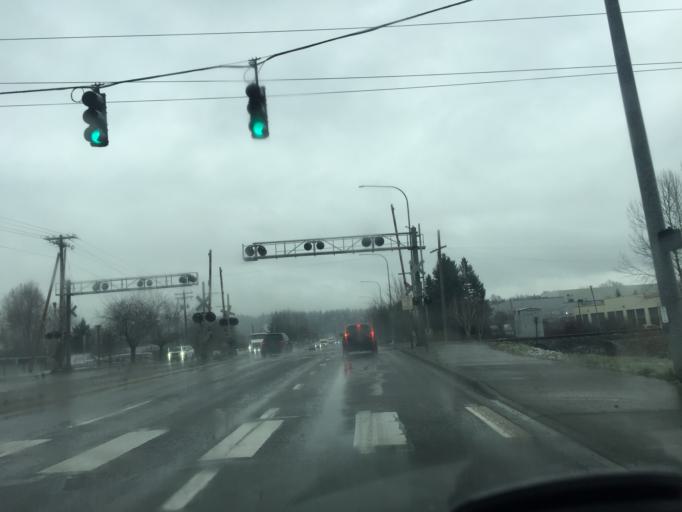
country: US
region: Washington
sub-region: King County
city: Kent
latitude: 47.4120
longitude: -122.2423
